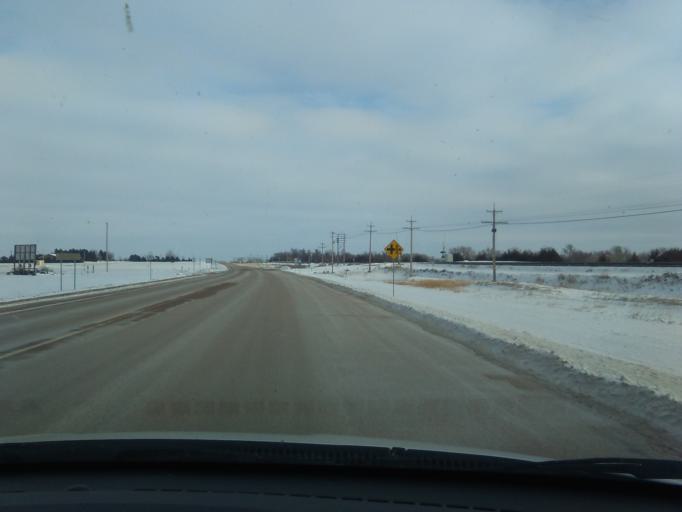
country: US
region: Nebraska
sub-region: Deuel County
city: Chappell
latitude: 41.1465
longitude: -102.6309
